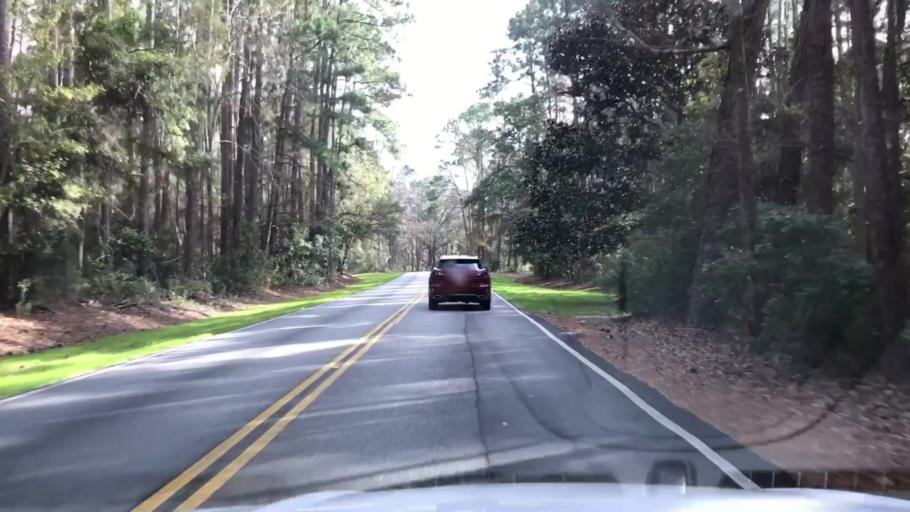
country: US
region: South Carolina
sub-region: Beaufort County
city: Hilton Head Island
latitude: 32.2262
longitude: -80.7238
